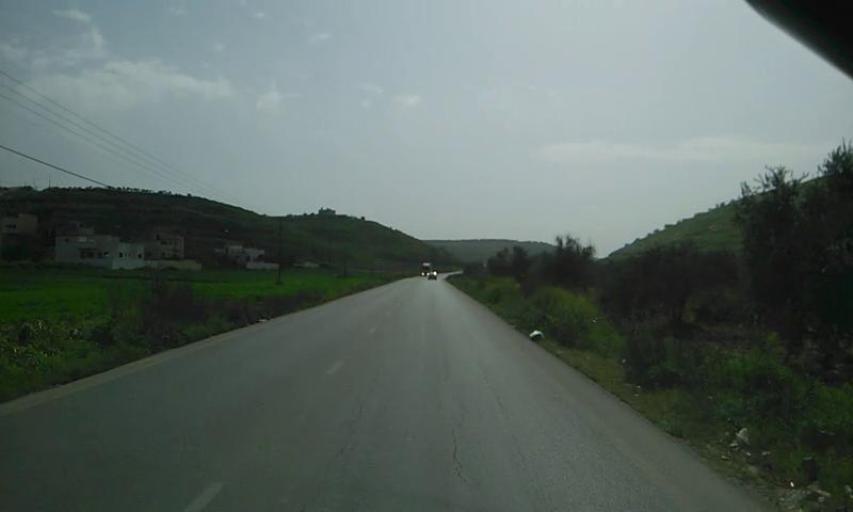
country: PS
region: West Bank
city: Mirkah
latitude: 32.3931
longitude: 35.2197
